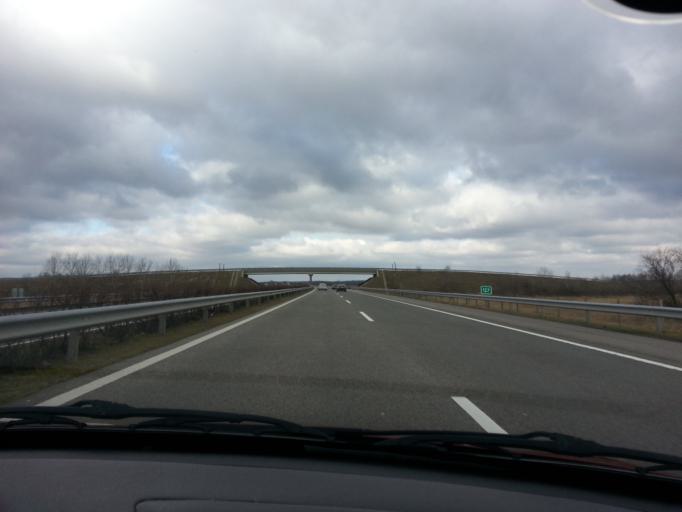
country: HU
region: Csongrad
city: Csengele
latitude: 46.5666
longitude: 19.8787
